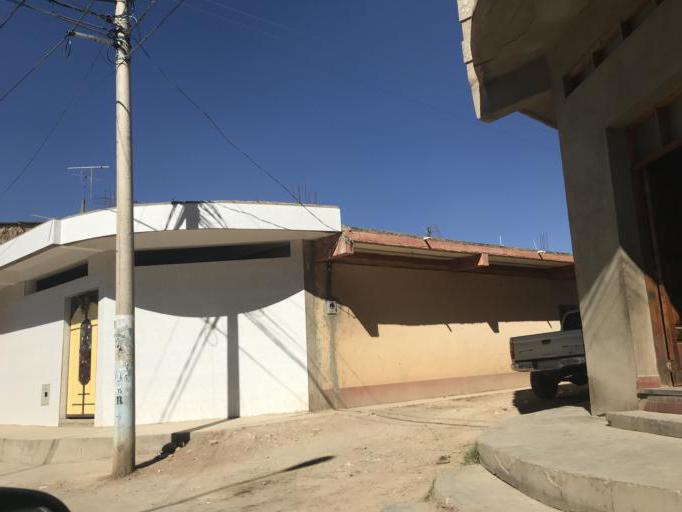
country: BO
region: Cochabamba
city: Cliza
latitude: -17.5934
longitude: -65.9367
